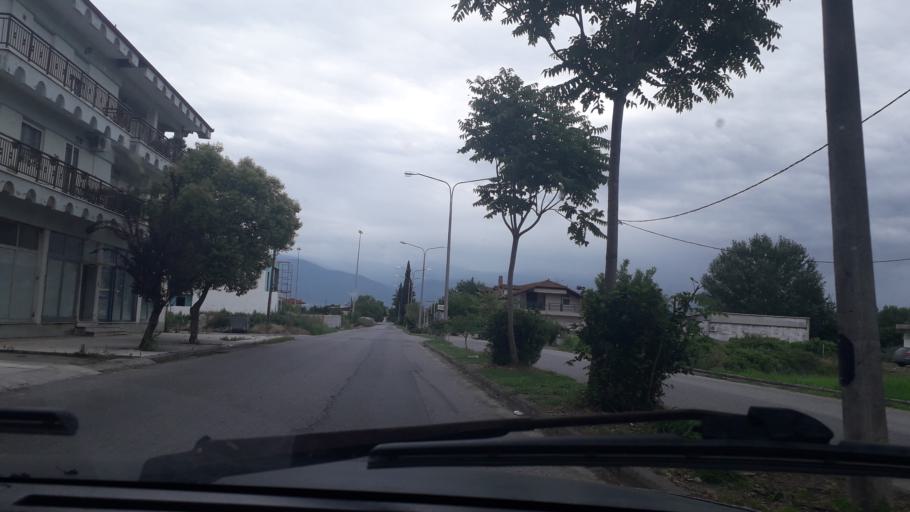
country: GR
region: Central Macedonia
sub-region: Nomos Pellis
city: Aridaia
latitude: 40.9677
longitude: 22.0623
